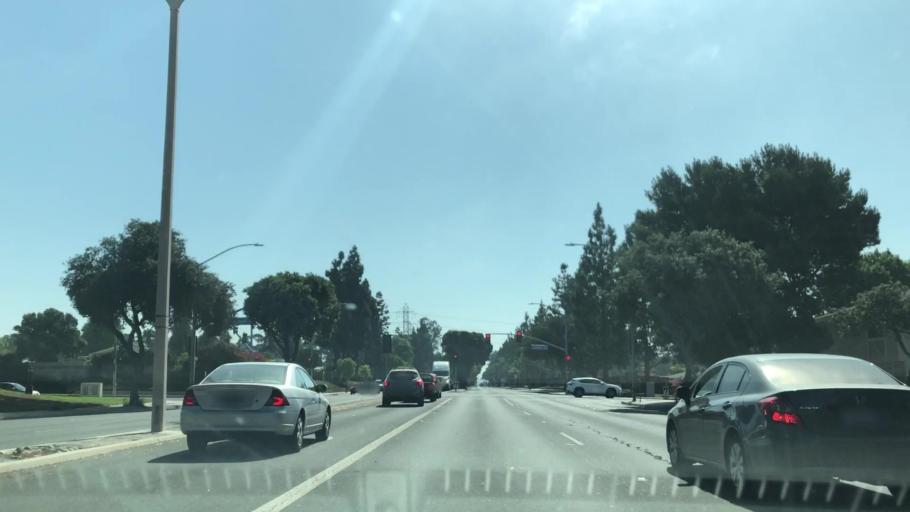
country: US
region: California
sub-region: Ventura County
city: El Rio
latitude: 34.2669
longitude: -119.2016
